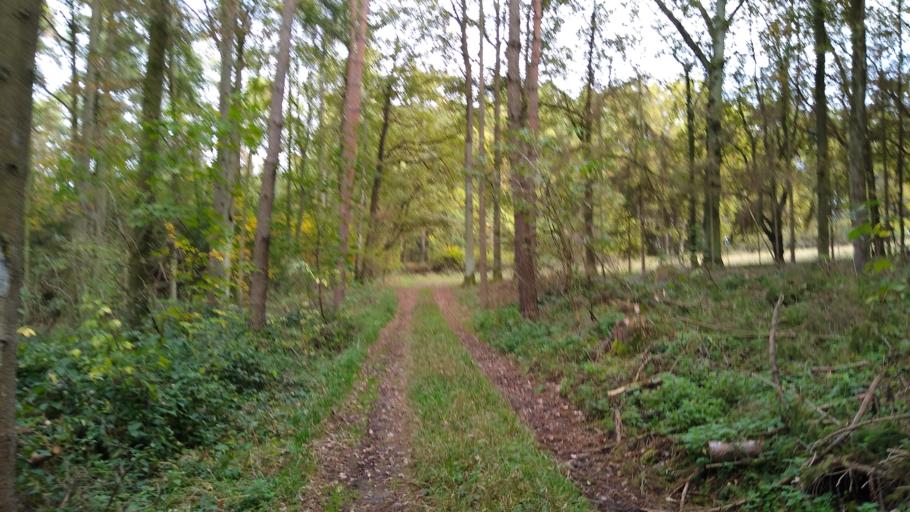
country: DE
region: Bavaria
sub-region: Regierungsbezirk Mittelfranken
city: Obermichelbach
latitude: 49.5048
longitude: 10.9248
